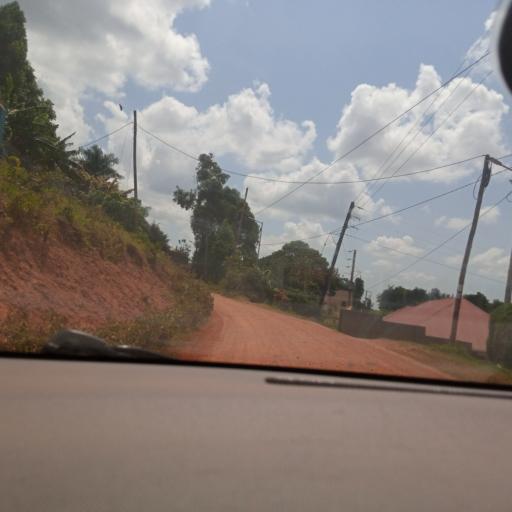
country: UG
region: Central Region
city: Masaka
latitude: -0.3260
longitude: 31.7409
